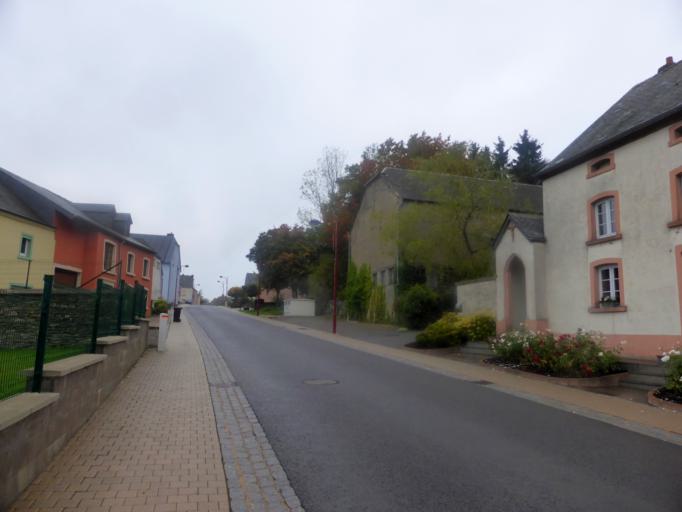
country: LU
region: Diekirch
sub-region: Canton de Wiltz
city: Boulaide
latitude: 49.8507
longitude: 5.7924
